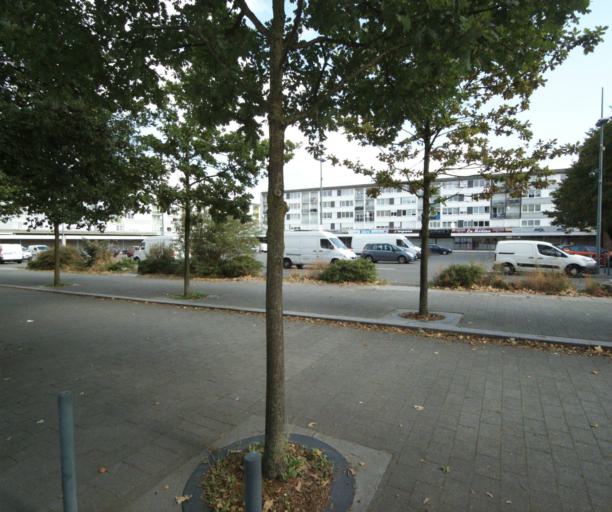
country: FR
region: Nord-Pas-de-Calais
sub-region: Departement du Nord
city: Villeneuve-d'Ascq
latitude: 50.6202
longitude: 3.1451
